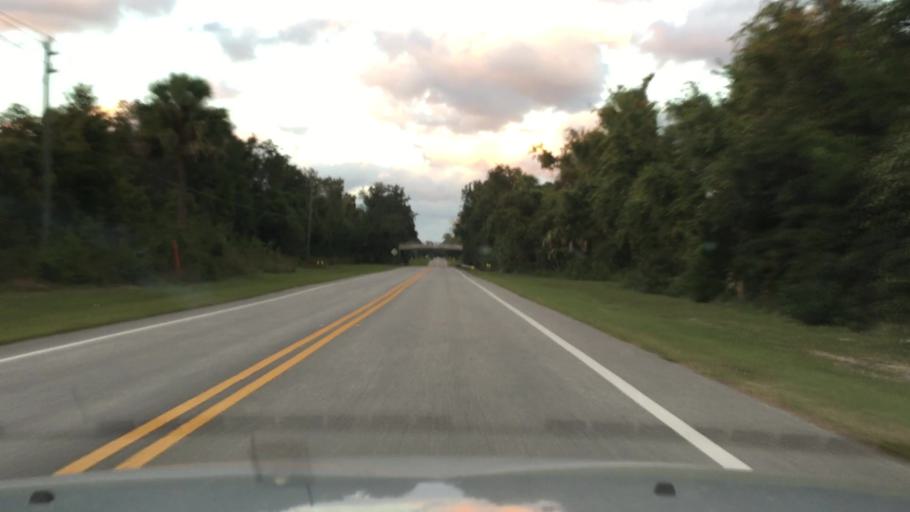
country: US
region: Florida
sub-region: Volusia County
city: Ormond Beach
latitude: 29.2932
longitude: -81.1087
